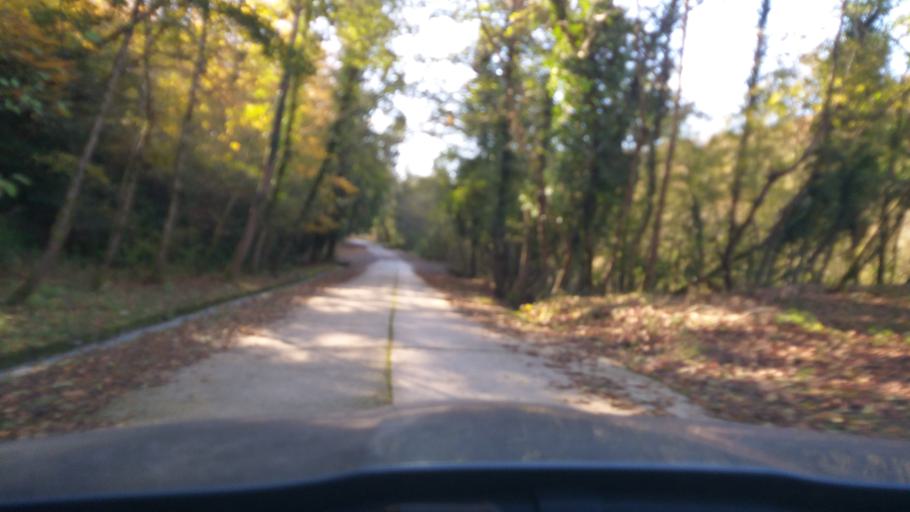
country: GE
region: Abkhazia
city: Bich'vinta
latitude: 43.1626
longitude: 40.4628
